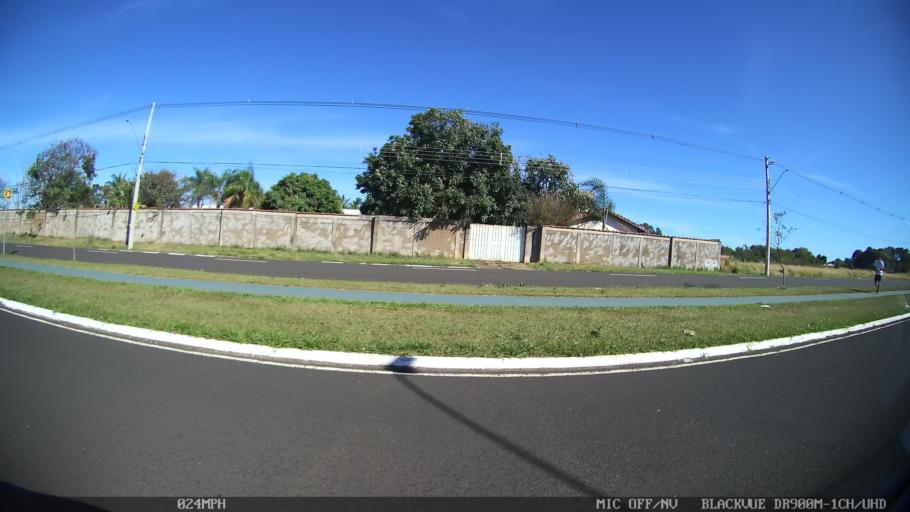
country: BR
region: Sao Paulo
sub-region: Franca
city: Franca
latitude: -20.5624
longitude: -47.3589
